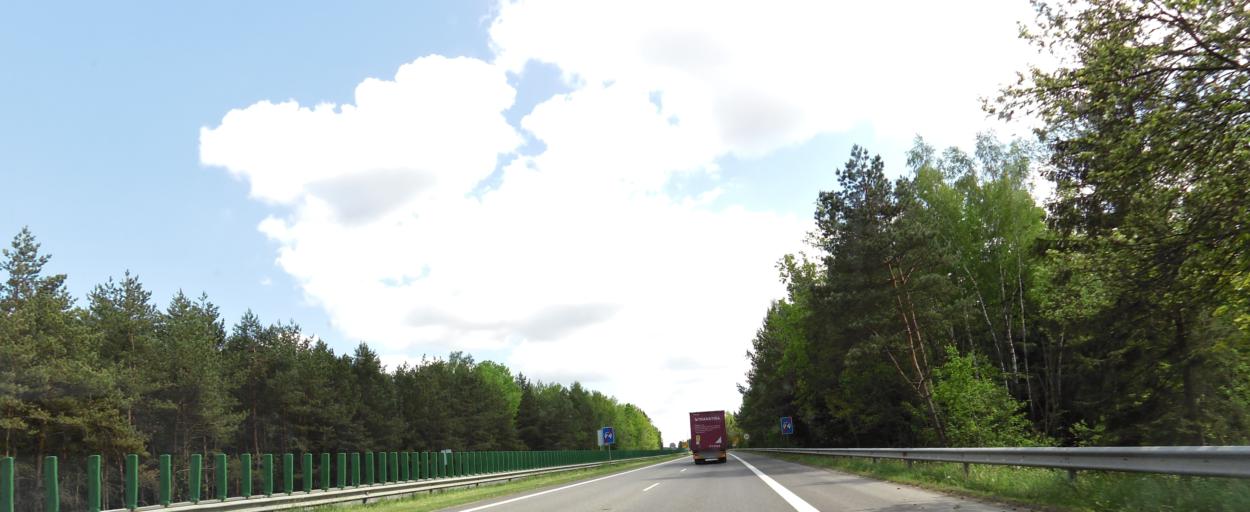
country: LT
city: Lentvaris
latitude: 54.6976
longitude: 25.0177
